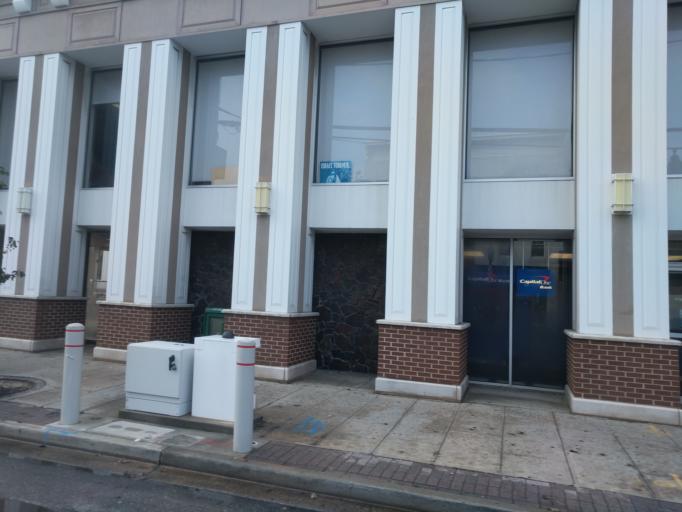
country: US
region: New York
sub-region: Nassau County
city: Cedarhurst
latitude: 40.6210
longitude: -73.7248
